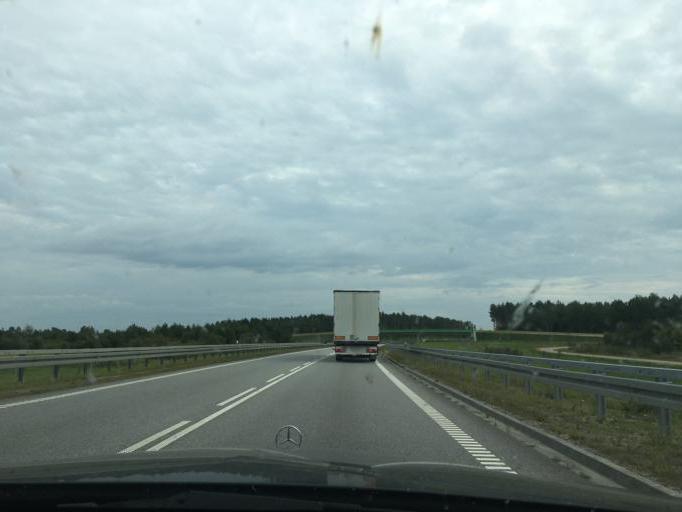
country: PL
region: Podlasie
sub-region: Powiat kolnenski
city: Stawiski
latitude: 53.3661
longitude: 22.1556
